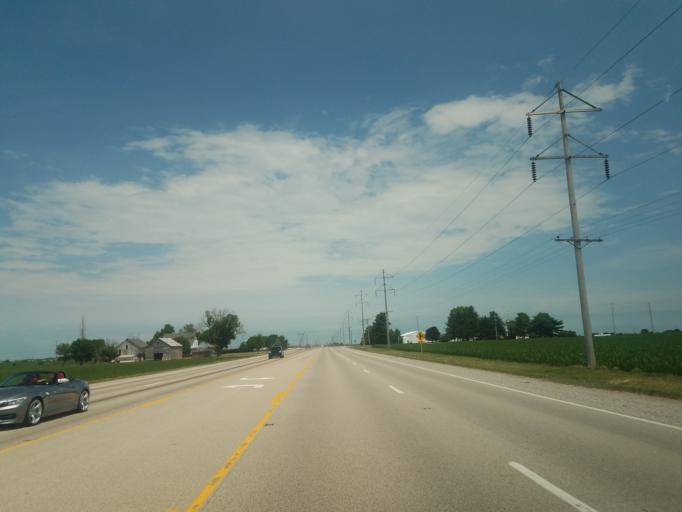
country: US
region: Illinois
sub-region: McLean County
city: Downs
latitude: 40.4413
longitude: -88.9016
